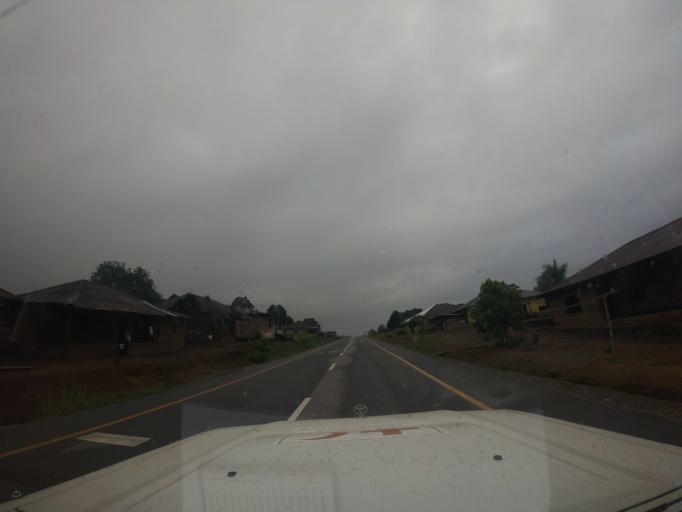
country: SL
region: Eastern Province
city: Hangha
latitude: 7.9573
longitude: -11.1373
